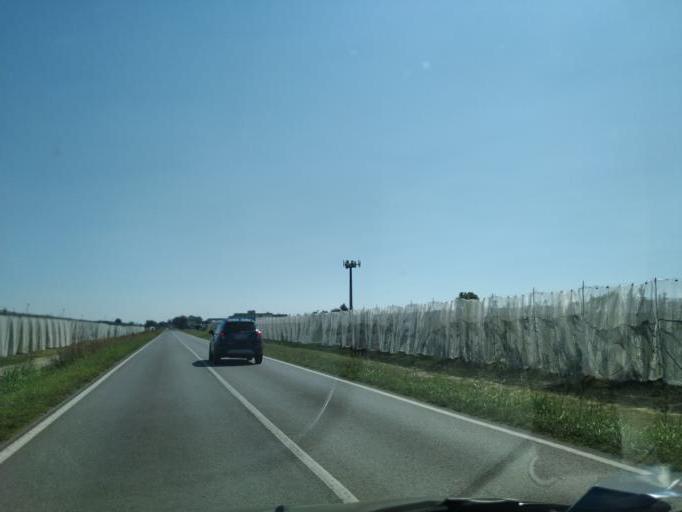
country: IT
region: Emilia-Romagna
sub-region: Provincia di Ferrara
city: La Saletta-Tamara
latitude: 44.8805
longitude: 11.7612
